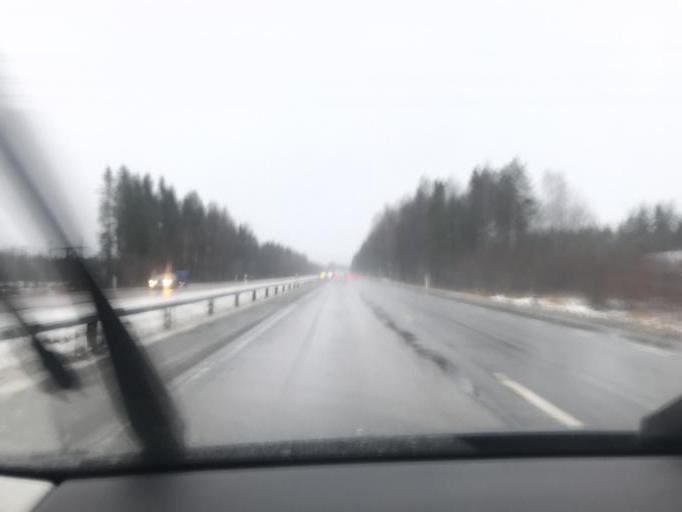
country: SE
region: Norrbotten
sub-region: Lulea Kommun
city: Bergnaset
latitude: 65.6208
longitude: 22.0743
